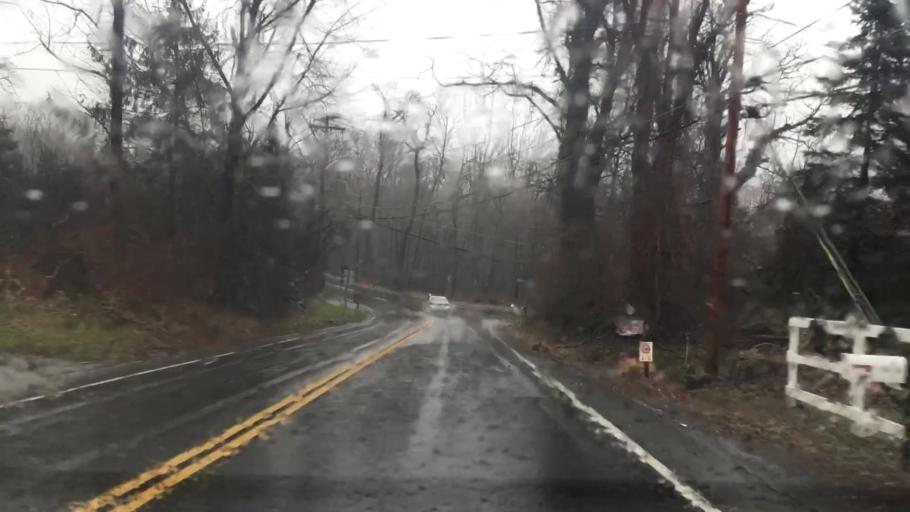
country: US
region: New York
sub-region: Putnam County
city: Putnam Lake
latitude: 41.4583
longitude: -73.5540
